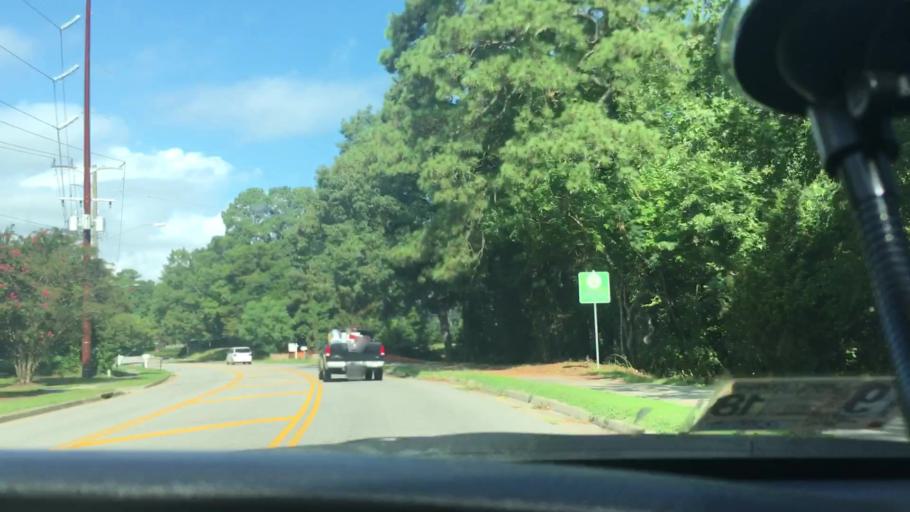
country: US
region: Virginia
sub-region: City of Virginia Beach
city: Virginia Beach
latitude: 36.8796
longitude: -76.0348
